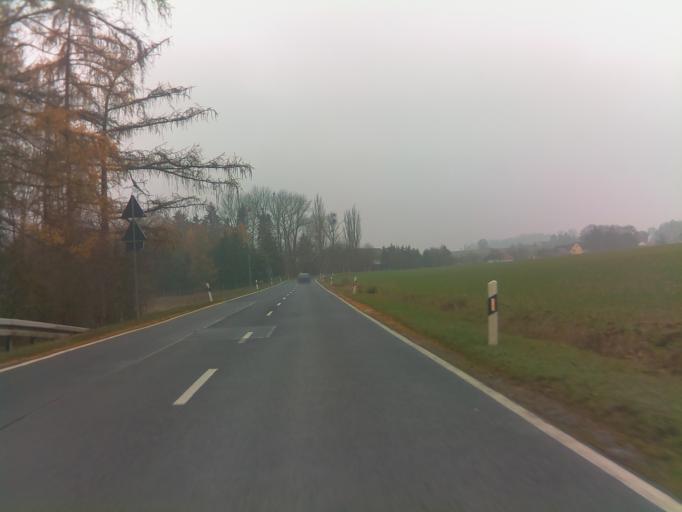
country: DE
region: Thuringia
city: Henfstadt
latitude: 50.4905
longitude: 10.5873
